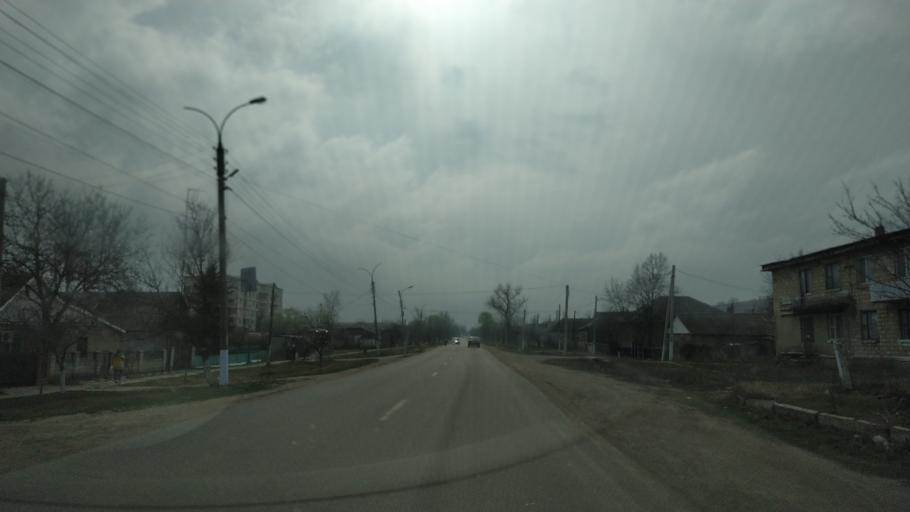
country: MD
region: Basarabeasca
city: Basarabeasca
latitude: 46.3423
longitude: 28.9525
